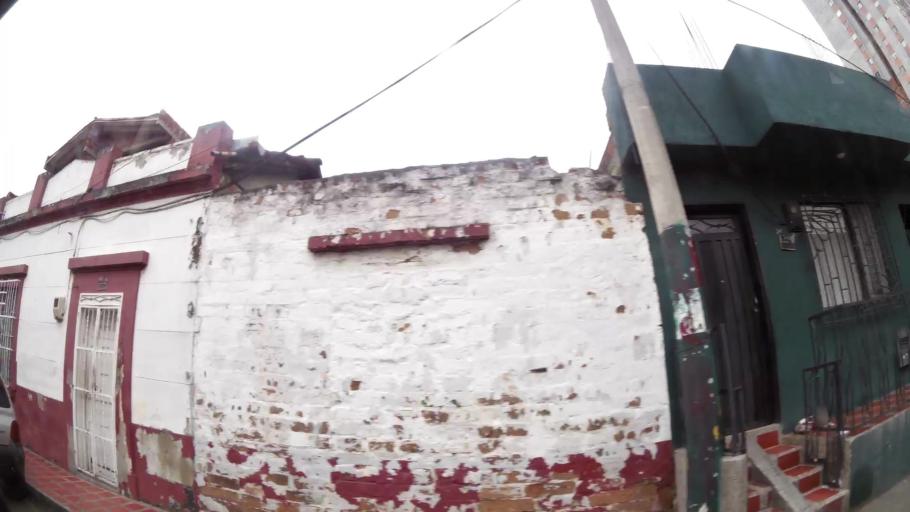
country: CO
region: Antioquia
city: Medellin
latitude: 6.2813
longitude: -75.5644
